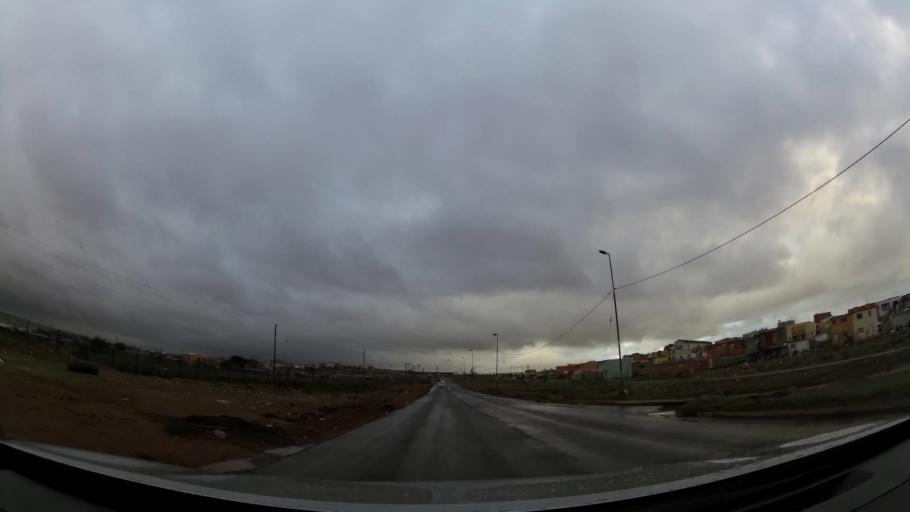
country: ZA
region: Eastern Cape
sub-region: Nelson Mandela Bay Metropolitan Municipality
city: Port Elizabeth
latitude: -33.8892
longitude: 25.5566
